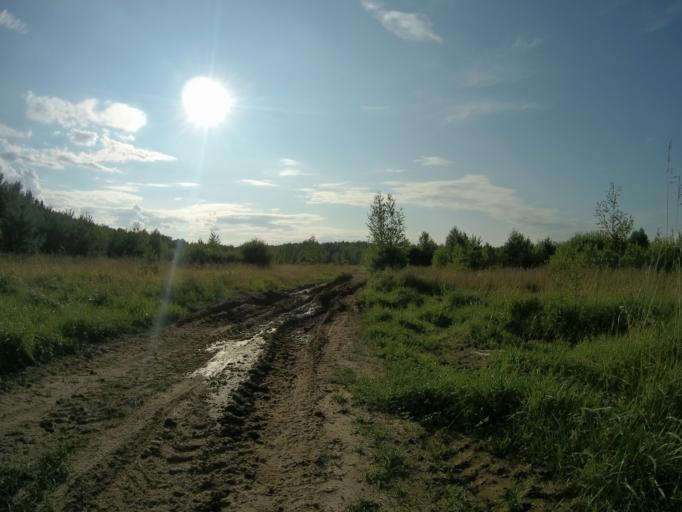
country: RU
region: Vladimir
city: Orgtrud
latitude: 56.1172
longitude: 40.6411
